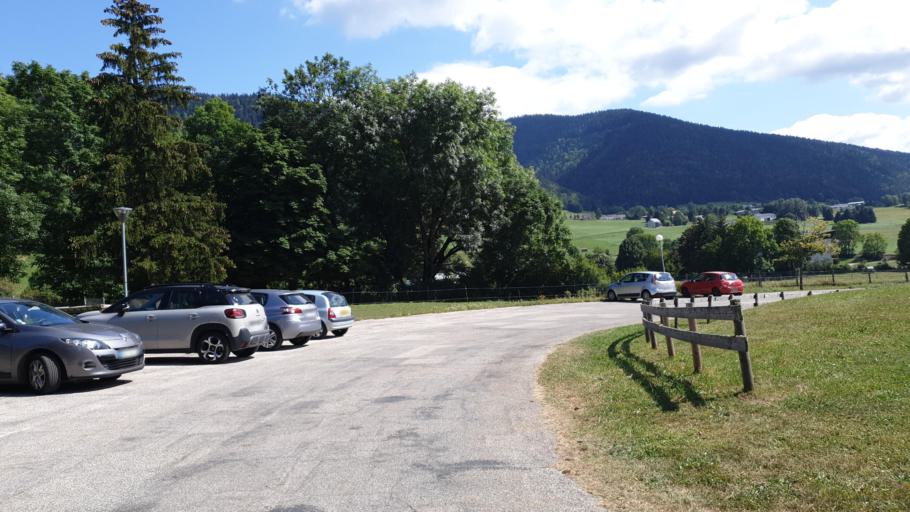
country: FR
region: Rhone-Alpes
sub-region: Departement de l'Isere
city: Autrans
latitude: 45.1836
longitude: 5.5550
